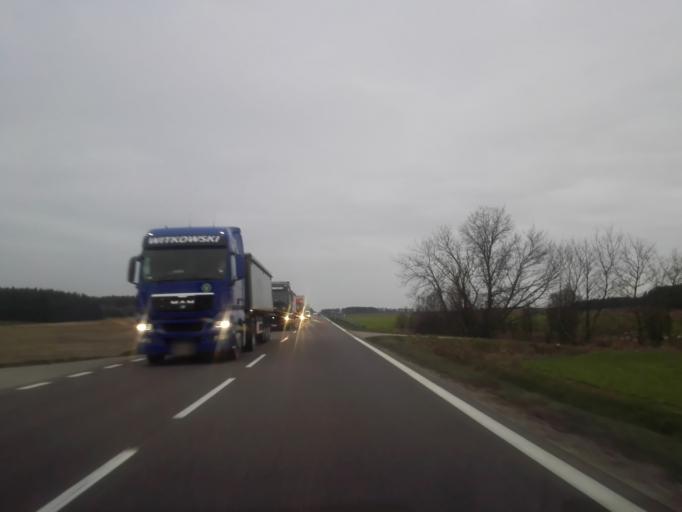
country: PL
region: Podlasie
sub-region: Powiat grajewski
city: Szczuczyn
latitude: 53.4824
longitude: 22.2159
